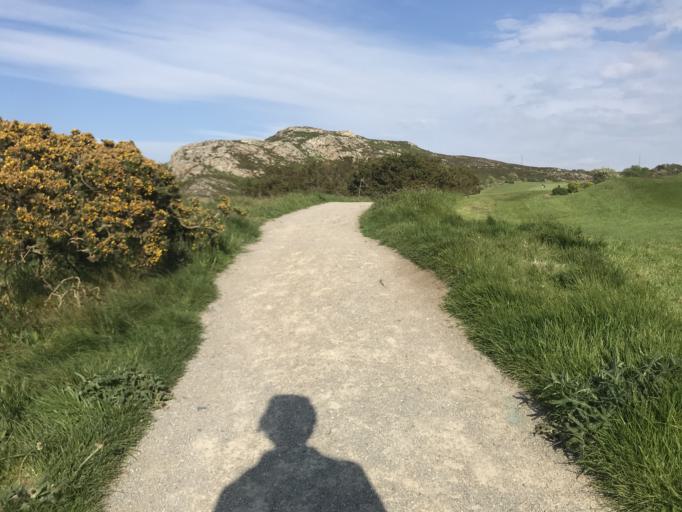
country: IE
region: Leinster
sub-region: Fingal County
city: Howth
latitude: 53.3752
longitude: -6.0825
